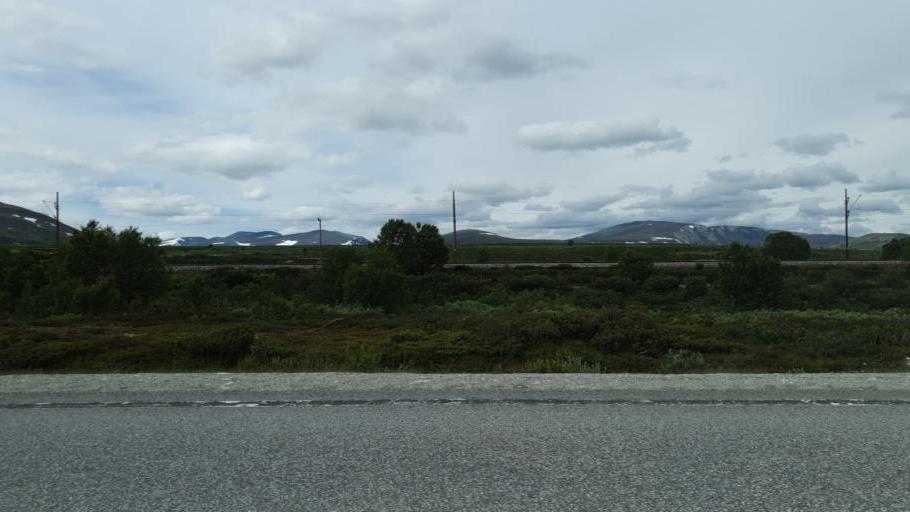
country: NO
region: Sor-Trondelag
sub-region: Oppdal
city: Oppdal
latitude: 62.2656
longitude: 9.5717
